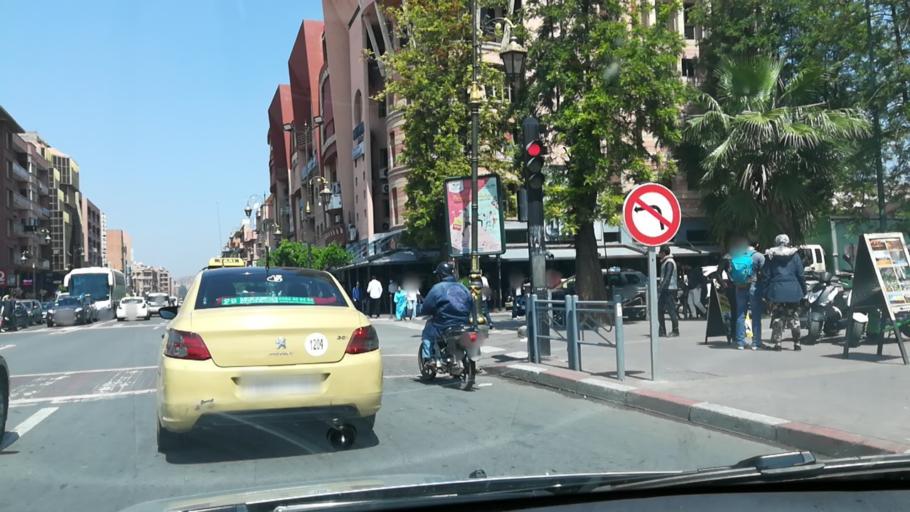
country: MA
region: Marrakech-Tensift-Al Haouz
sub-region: Marrakech
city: Marrakesh
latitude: 31.6332
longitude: -8.0094
